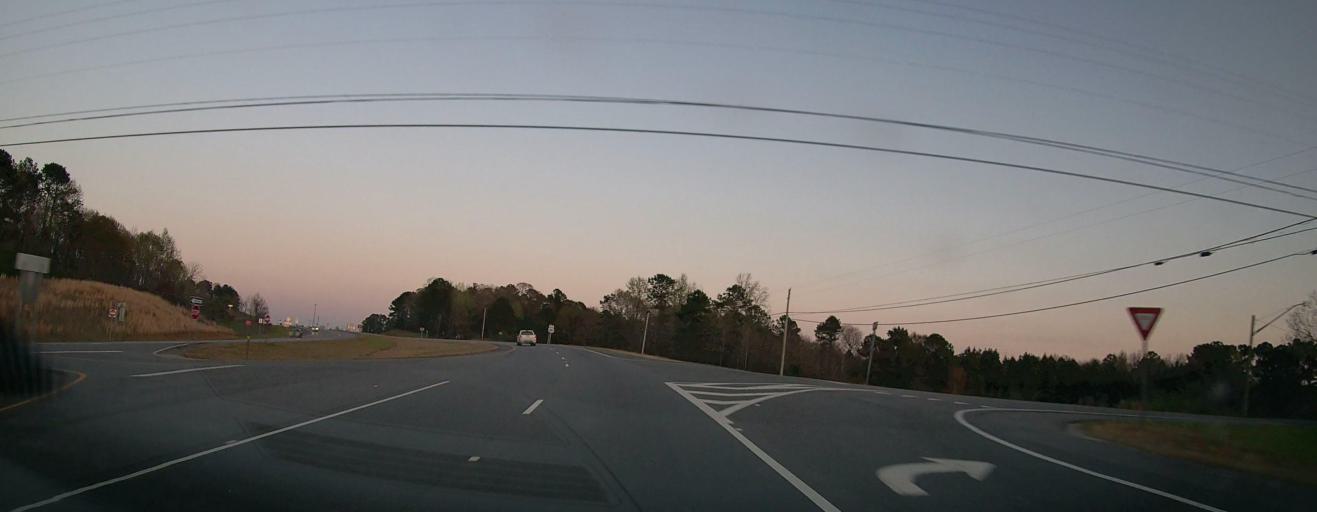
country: US
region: Alabama
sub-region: Tallapoosa County
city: Alexander City
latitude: 32.8866
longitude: -85.8720
